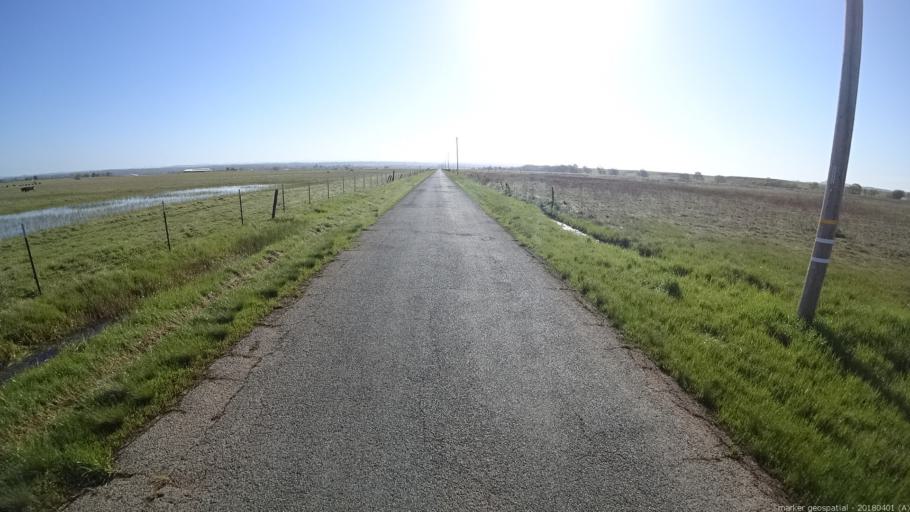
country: US
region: California
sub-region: Sacramento County
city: Rancho Murieta
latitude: 38.4204
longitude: -121.0414
